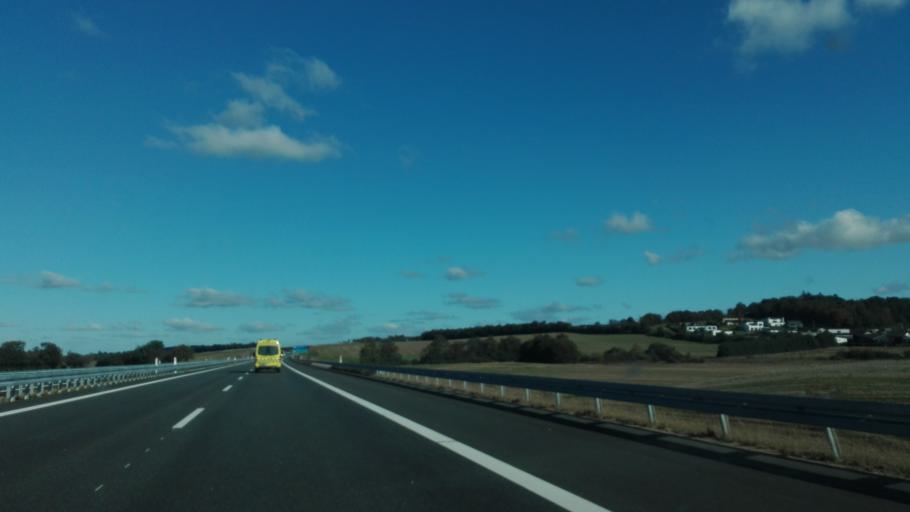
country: DK
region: Central Jutland
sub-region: Silkeborg Kommune
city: Silkeborg
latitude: 56.1838
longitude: 9.4875
